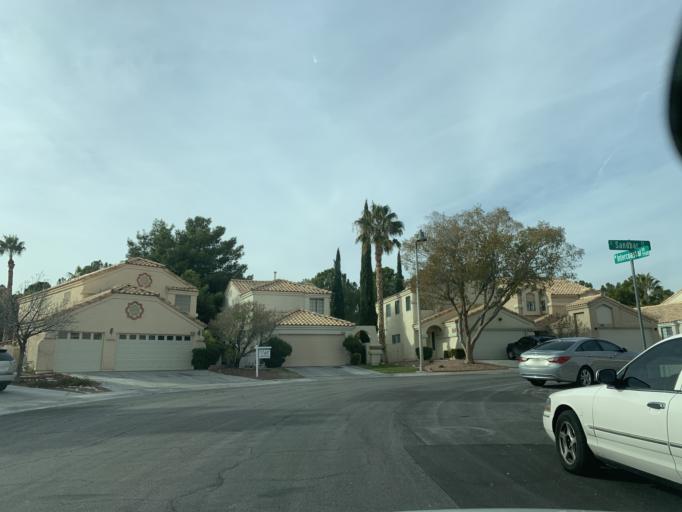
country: US
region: Nevada
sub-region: Clark County
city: Summerlin South
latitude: 36.1363
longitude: -115.3051
